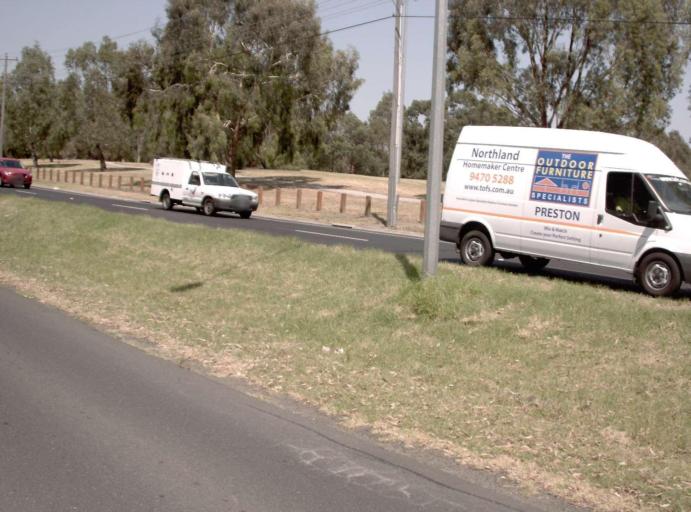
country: AU
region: Victoria
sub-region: Manningham
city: Bulleen
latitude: -37.7744
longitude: 145.0789
